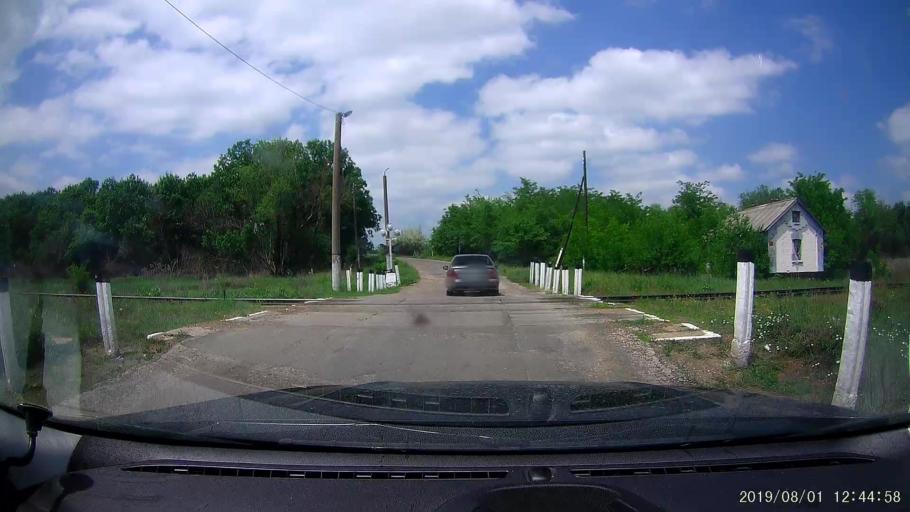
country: UA
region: Odessa
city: Vynohradivka
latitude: 45.6975
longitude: 28.5013
